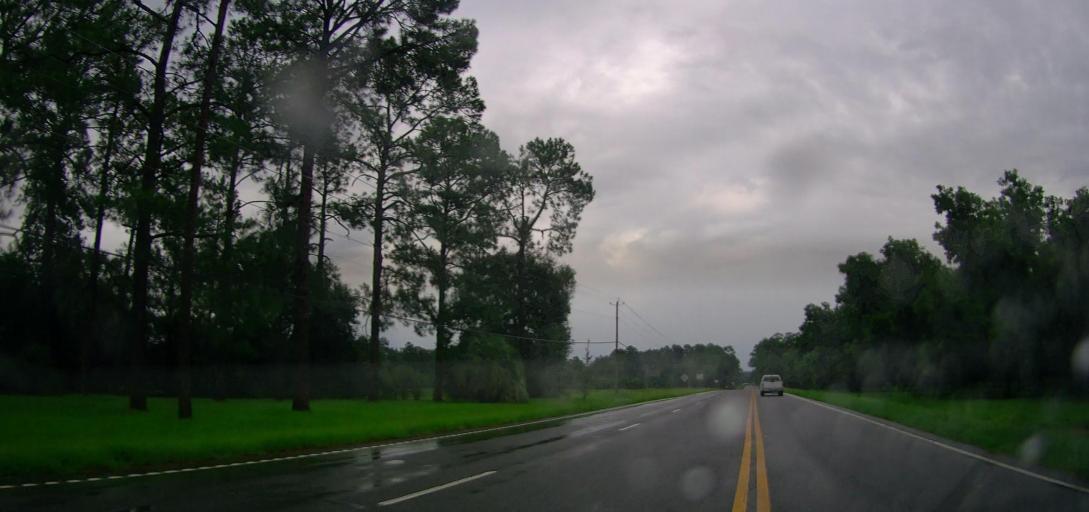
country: US
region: Georgia
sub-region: Ware County
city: Deenwood
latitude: 31.2625
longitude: -82.3904
